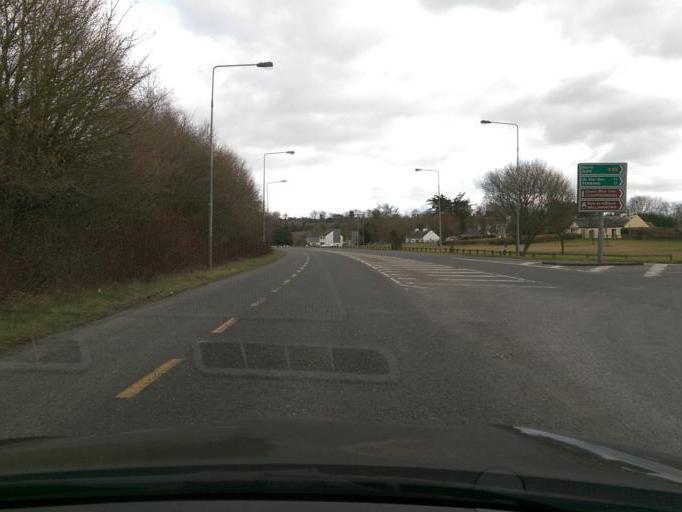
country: IE
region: Leinster
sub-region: An Iarmhi
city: Athlone
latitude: 53.4024
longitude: -7.8788
